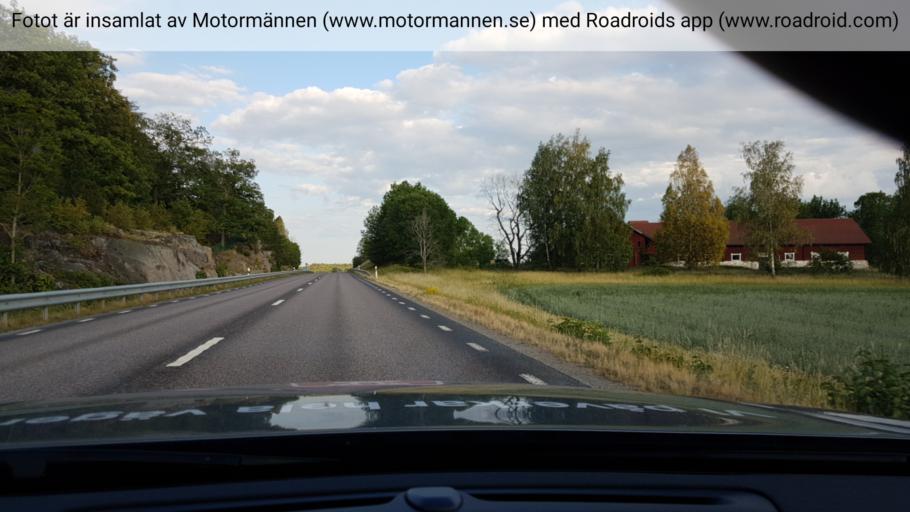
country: SE
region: Uppsala
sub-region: Enkopings Kommun
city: Orsundsbro
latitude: 59.8768
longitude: 17.2878
